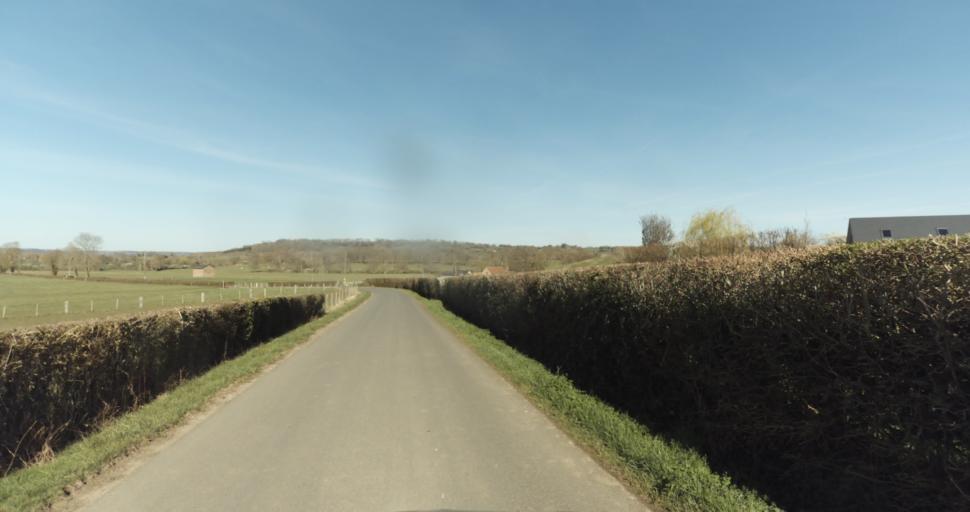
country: FR
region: Lower Normandy
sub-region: Departement du Calvados
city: Saint-Pierre-sur-Dives
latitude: 49.0228
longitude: 0.0541
